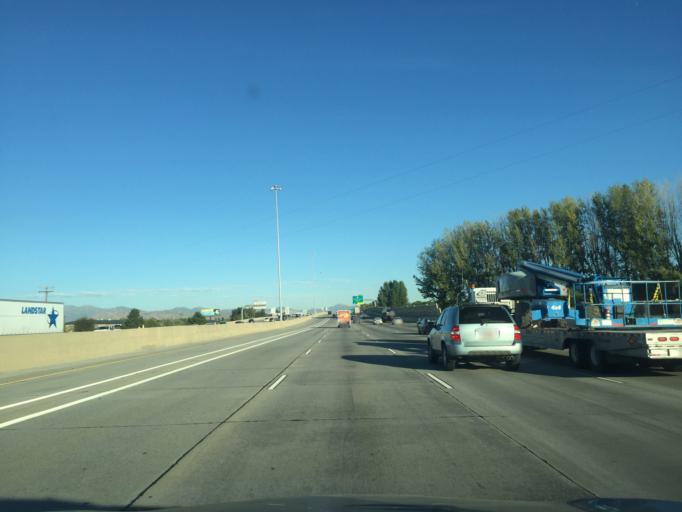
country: US
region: Utah
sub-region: Utah County
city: American Fork
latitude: 40.3641
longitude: -111.7907
